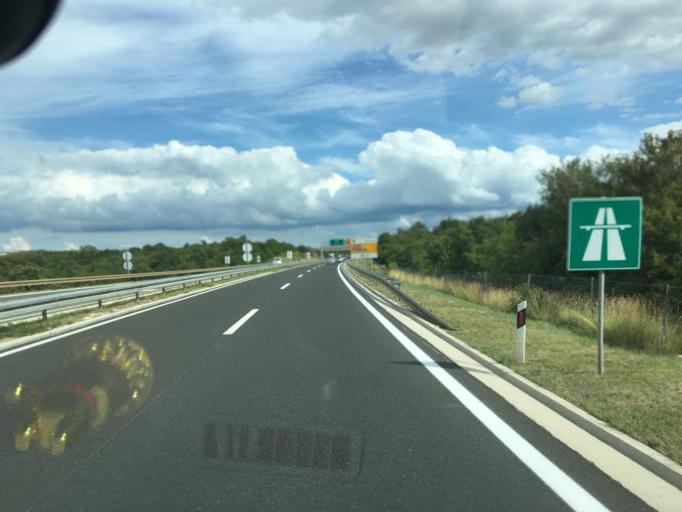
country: HR
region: Istarska
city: Vodnjan
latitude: 45.1182
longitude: 13.8085
